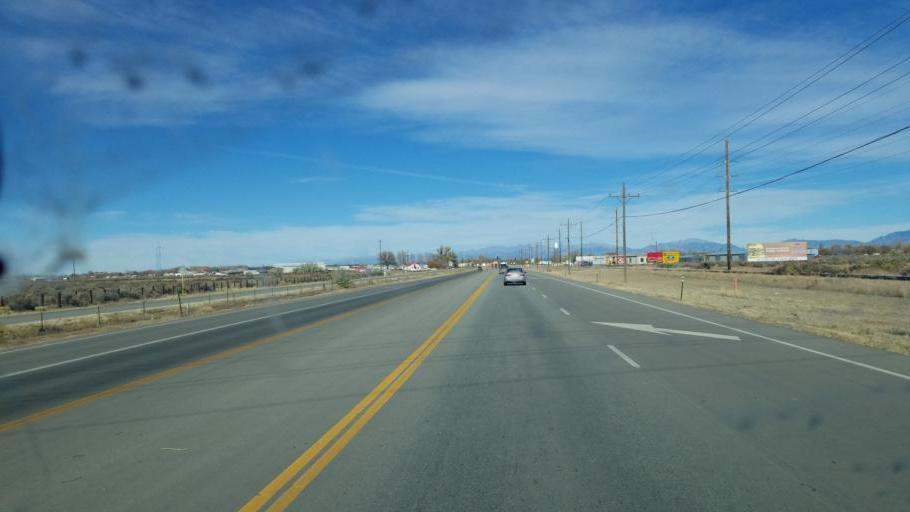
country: US
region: Colorado
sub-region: Alamosa County
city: Alamosa
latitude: 37.4513
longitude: -105.8796
